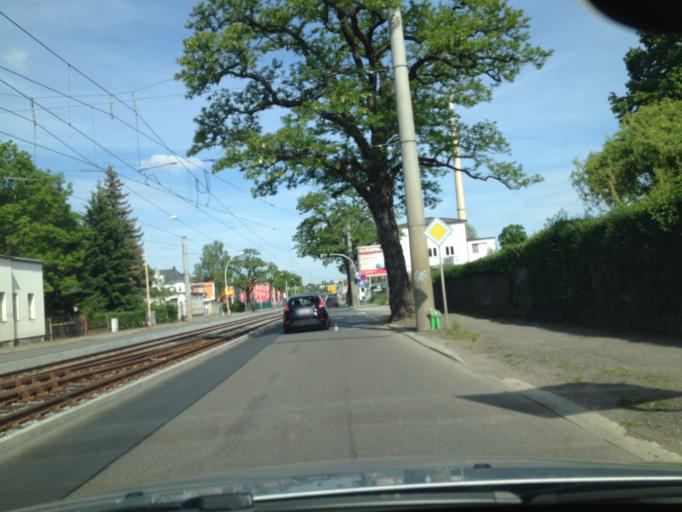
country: DE
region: Saxony
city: Chemnitz
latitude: 50.7933
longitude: 12.9240
